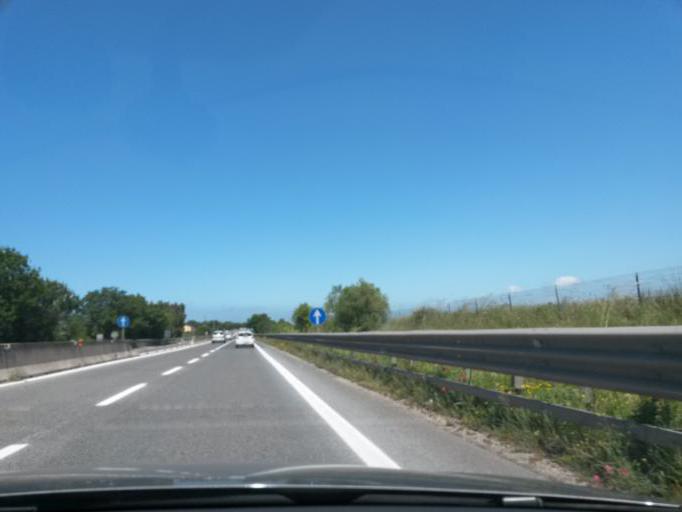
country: IT
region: Tuscany
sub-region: Provincia di Livorno
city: Cecina
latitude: 43.3083
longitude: 10.5417
